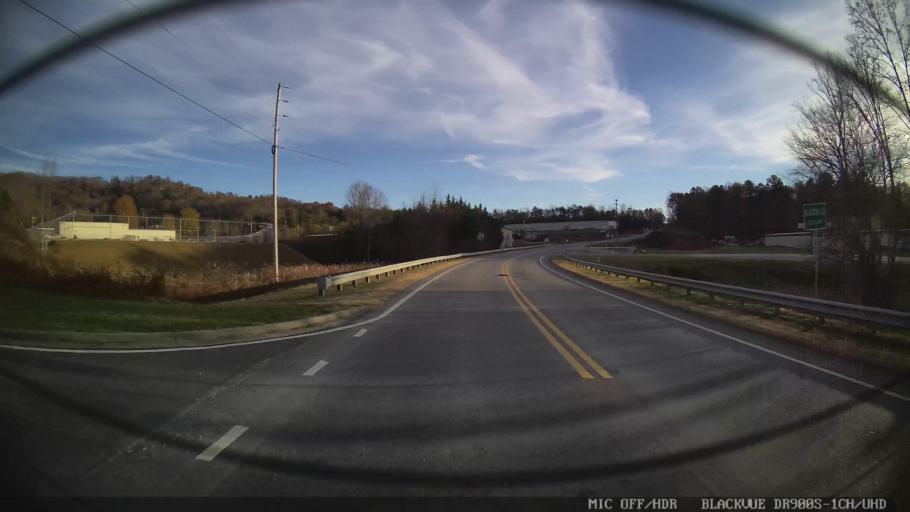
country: US
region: Georgia
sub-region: Union County
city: Blairsville
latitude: 34.8764
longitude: -83.9465
